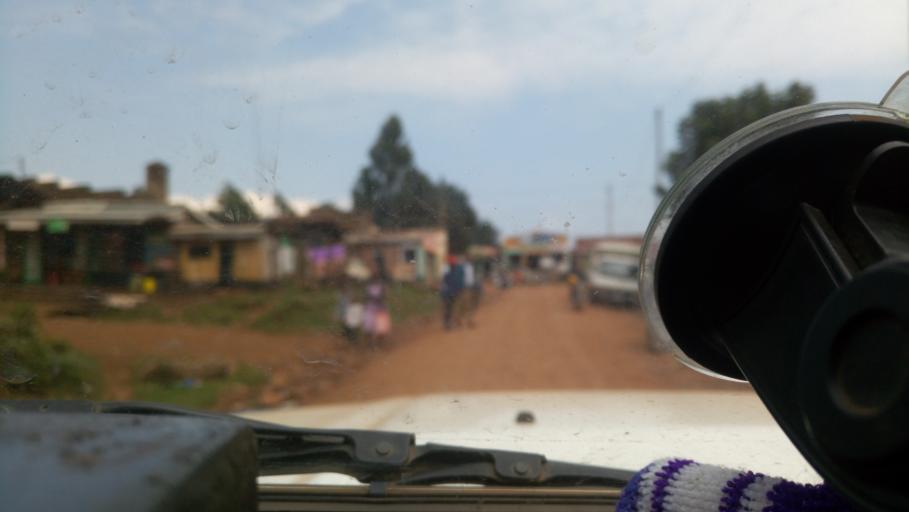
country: KE
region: Kericho
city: Litein
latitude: -0.6279
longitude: 35.1965
